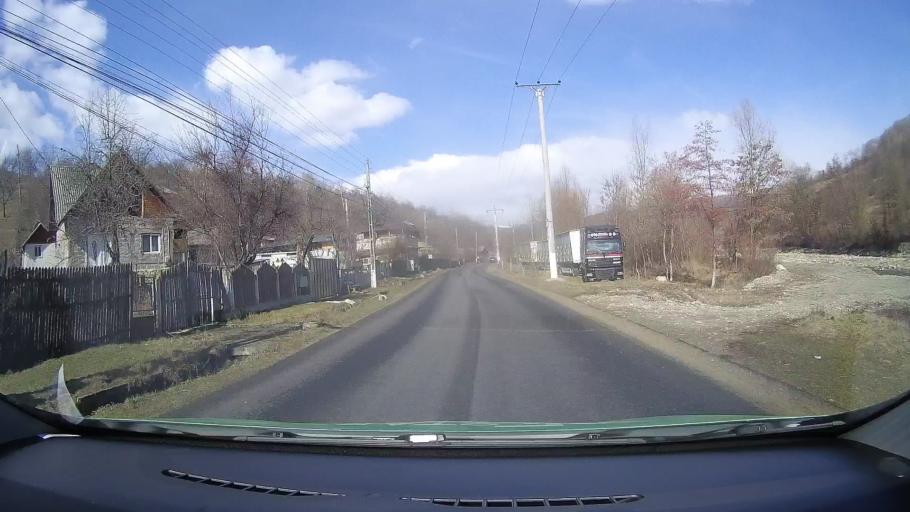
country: RO
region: Dambovita
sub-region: Comuna Runcu
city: Badeni
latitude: 45.1634
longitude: 25.3962
